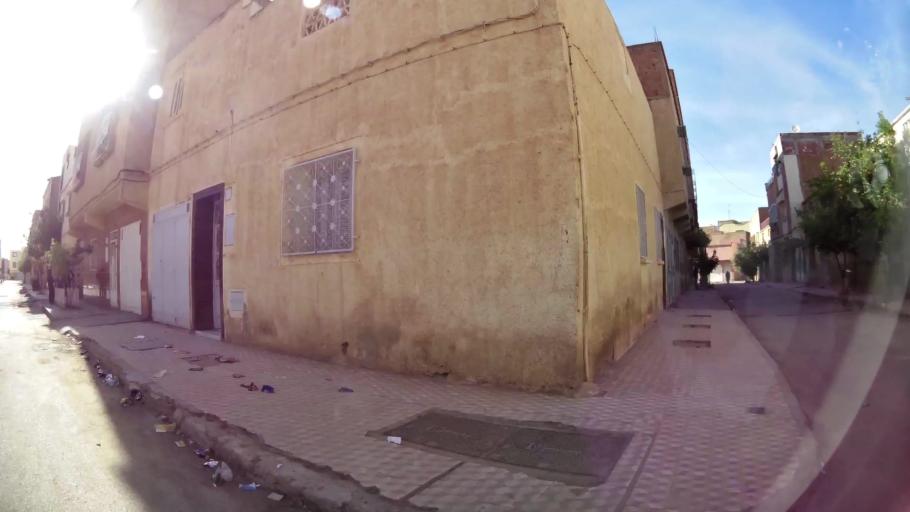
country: MA
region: Oriental
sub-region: Oujda-Angad
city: Oujda
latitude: 34.6729
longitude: -1.8943
